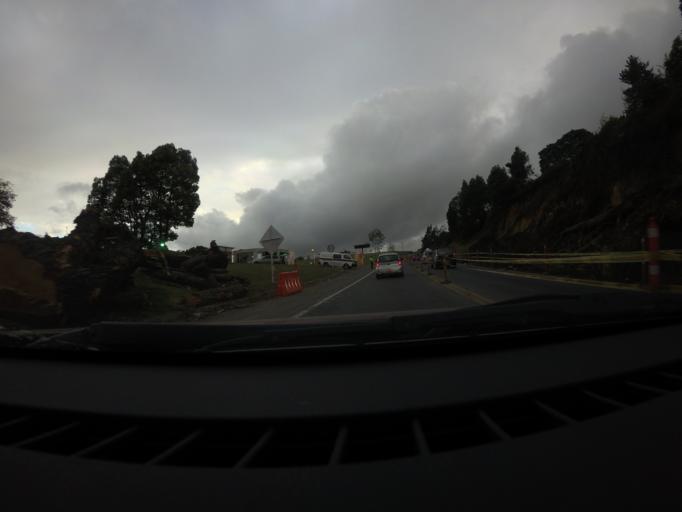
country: CO
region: Boyaca
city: Samaca
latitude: 5.4497
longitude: -73.4321
